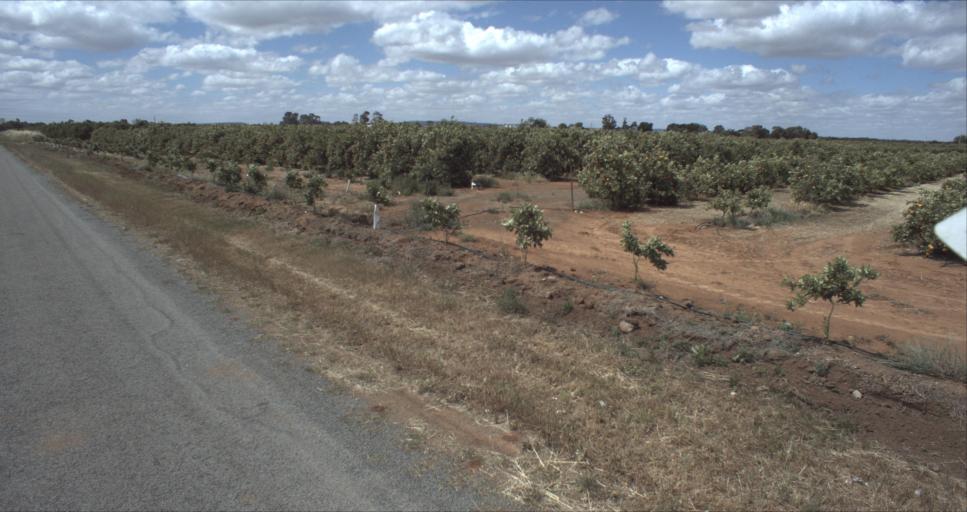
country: AU
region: New South Wales
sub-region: Leeton
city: Leeton
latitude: -34.5834
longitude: 146.3918
